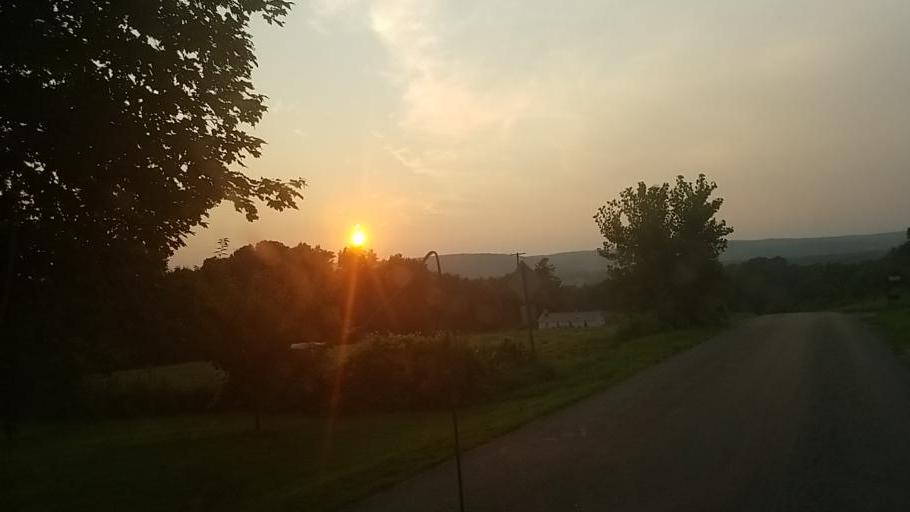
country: US
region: New York
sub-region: Montgomery County
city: Fonda
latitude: 42.9183
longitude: -74.4093
